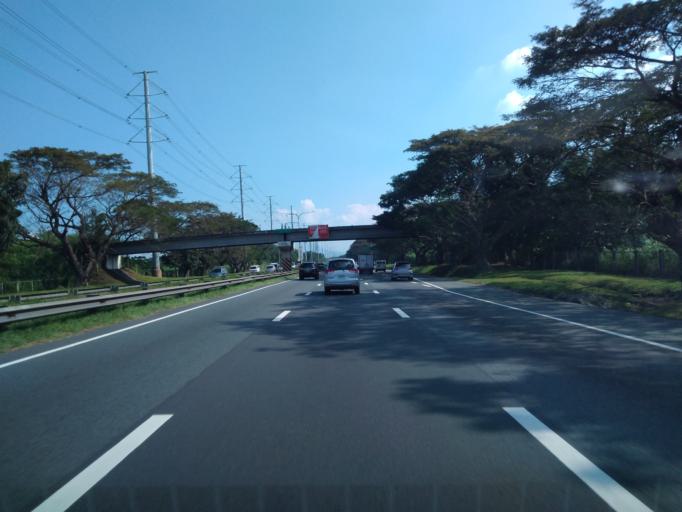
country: PH
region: Calabarzon
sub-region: Province of Laguna
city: Cabuyao
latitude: 14.2613
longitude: 121.1012
